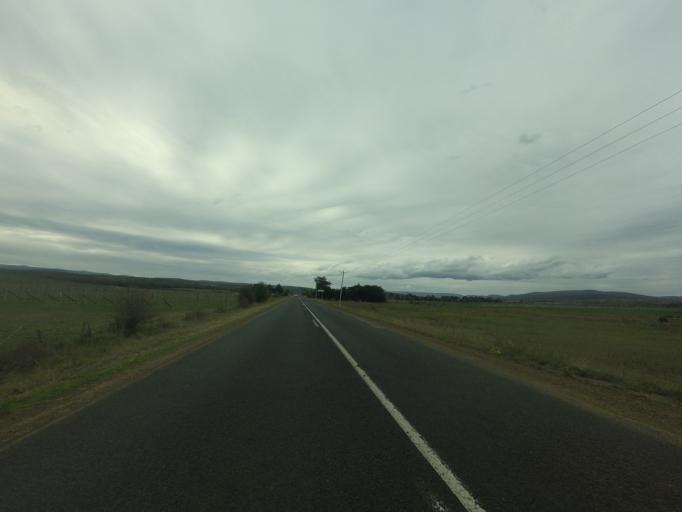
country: AU
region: Tasmania
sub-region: Break O'Day
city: St Helens
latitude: -42.0048
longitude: 148.0686
